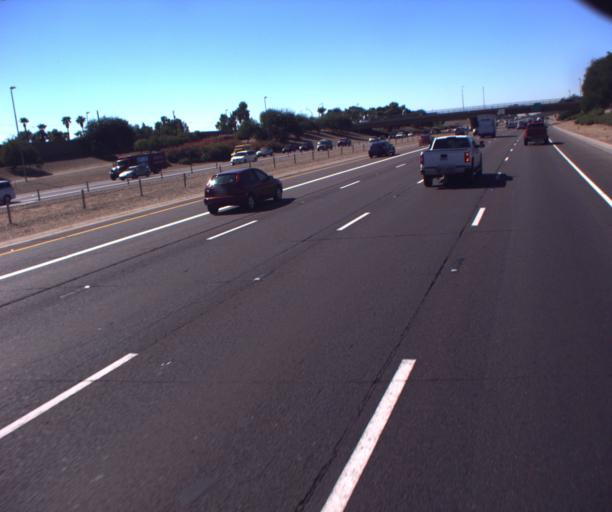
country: US
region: Arizona
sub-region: Maricopa County
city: Phoenix
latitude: 33.4620
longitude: -112.1490
